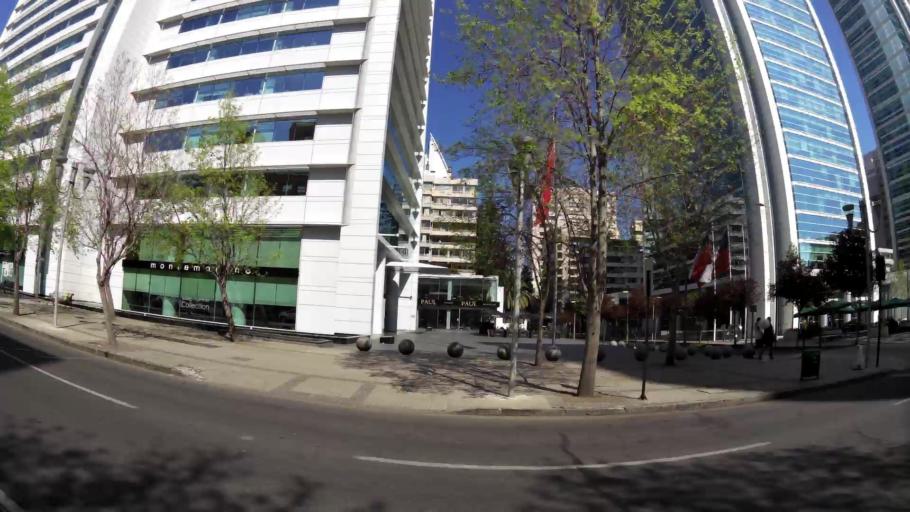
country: CL
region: Santiago Metropolitan
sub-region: Provincia de Santiago
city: Villa Presidente Frei, Nunoa, Santiago, Chile
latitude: -33.4142
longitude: -70.5934
